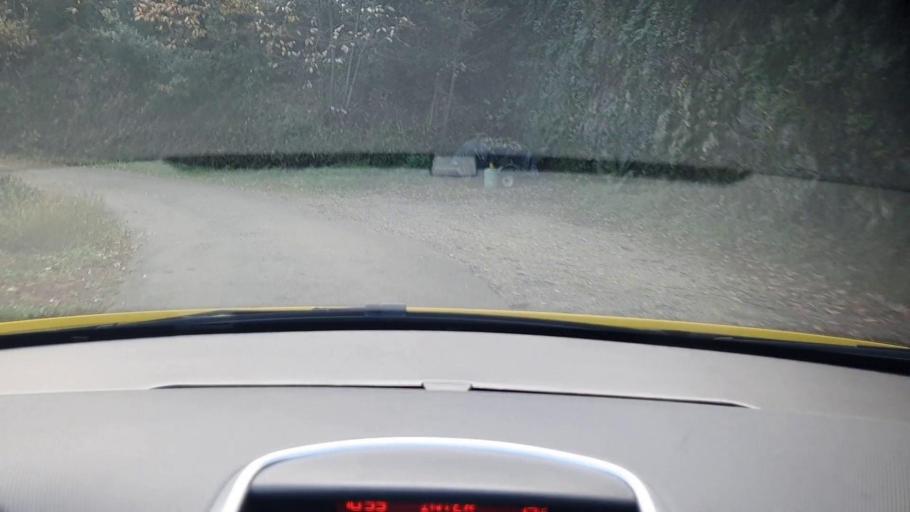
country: FR
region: Languedoc-Roussillon
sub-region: Departement du Gard
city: Lasalle
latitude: 44.0527
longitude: 3.8286
